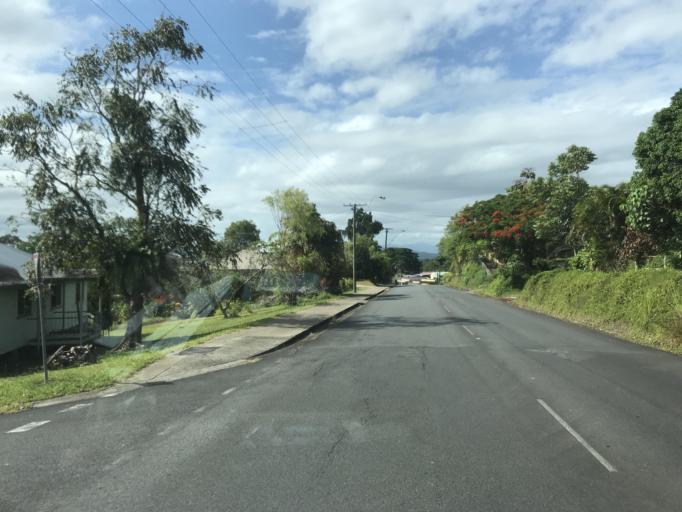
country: AU
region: Queensland
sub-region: Cassowary Coast
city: Innisfail
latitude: -17.5317
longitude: 146.0338
